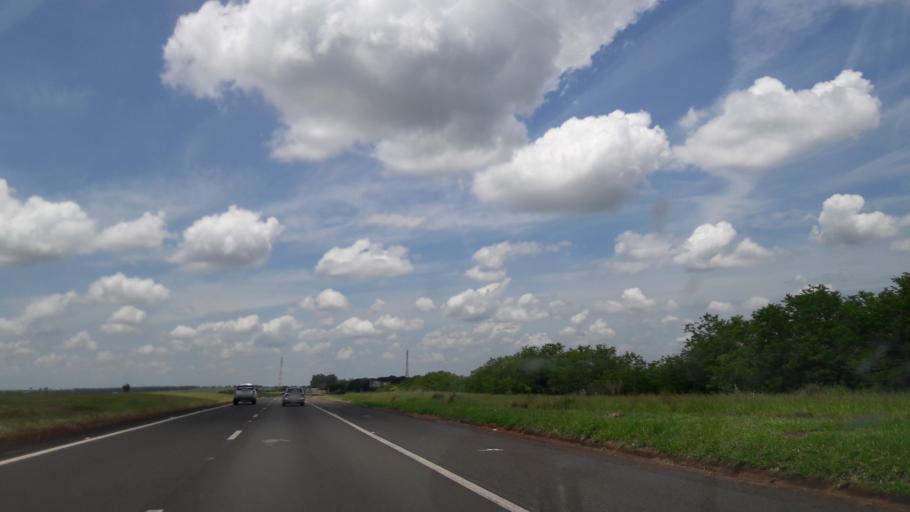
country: BR
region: Sao Paulo
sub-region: Avare
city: Avare
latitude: -22.9566
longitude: -48.8486
